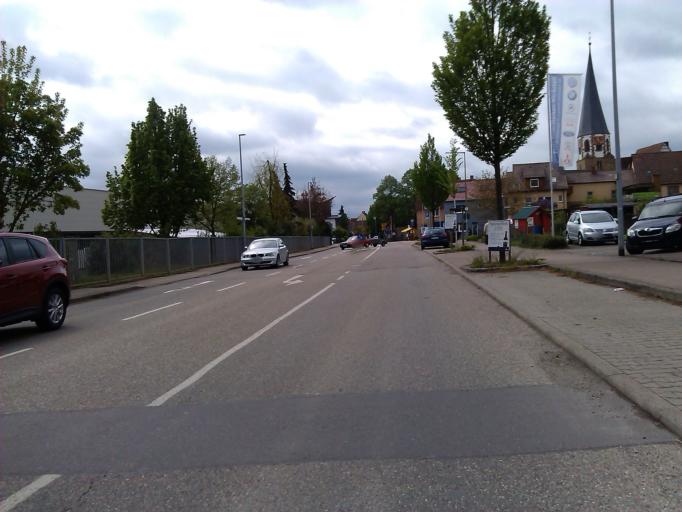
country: DE
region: Baden-Wuerttemberg
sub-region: Regierungsbezirk Stuttgart
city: Brackenheim
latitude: 49.0806
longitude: 9.0670
